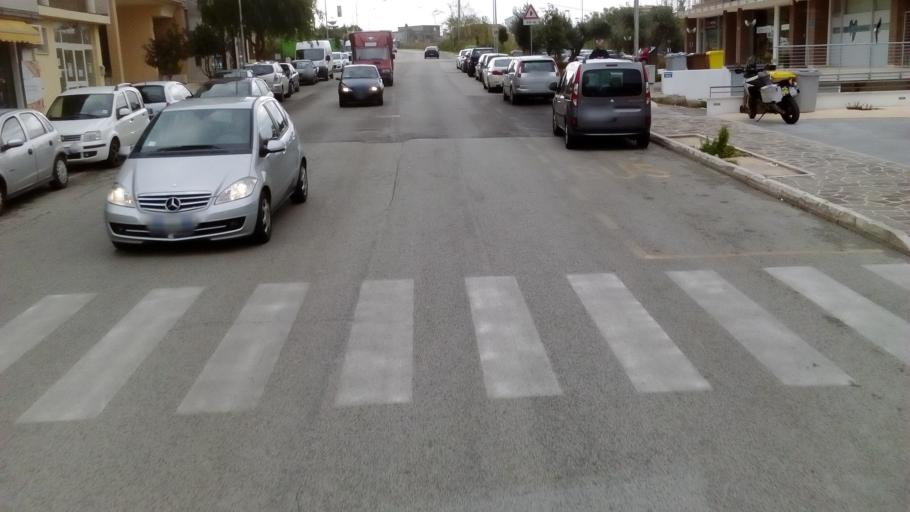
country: IT
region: Abruzzo
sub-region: Provincia di Chieti
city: Vasto
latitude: 42.1042
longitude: 14.7022
